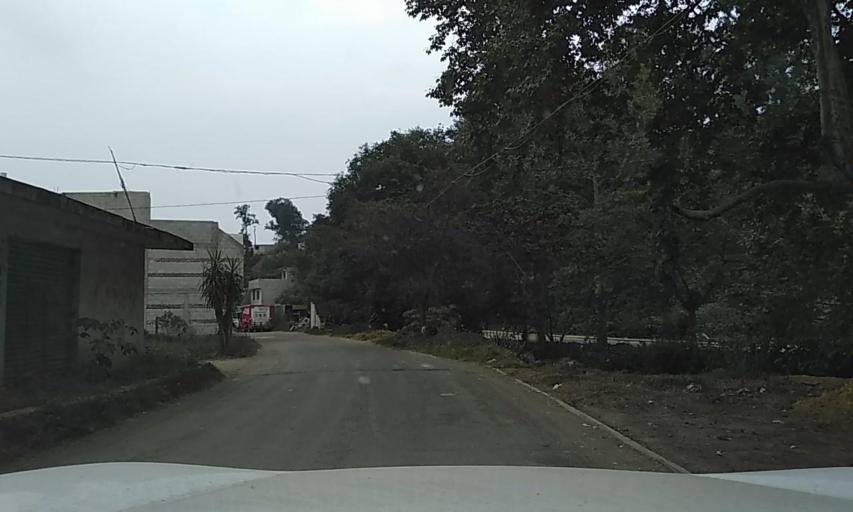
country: MX
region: Veracruz
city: El Castillo
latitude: 19.5715
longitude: -96.8921
